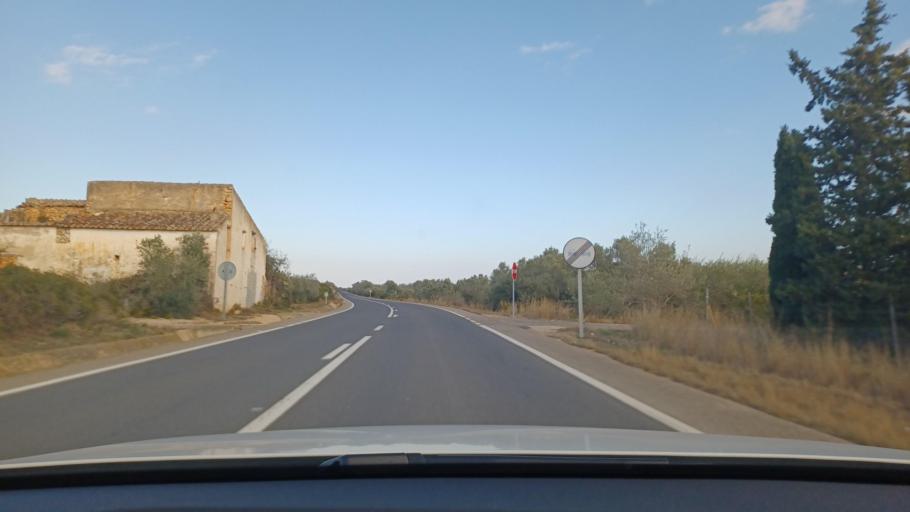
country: ES
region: Catalonia
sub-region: Provincia de Tarragona
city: Ulldecona
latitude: 40.6488
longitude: 0.3900
